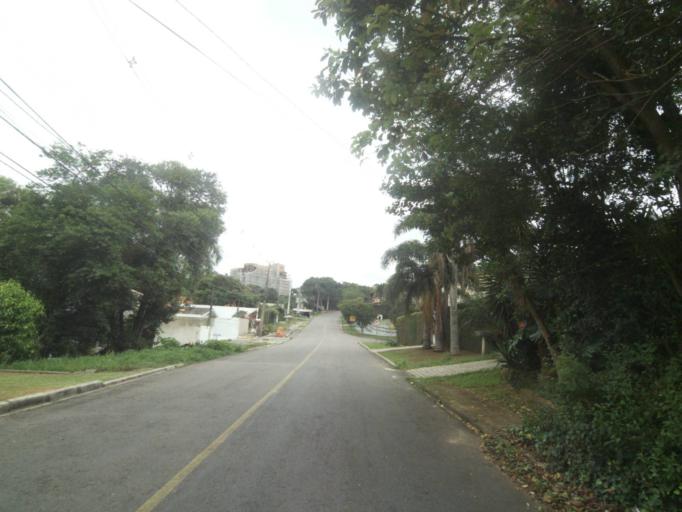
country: BR
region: Parana
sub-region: Curitiba
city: Curitiba
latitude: -25.3986
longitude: -49.2845
